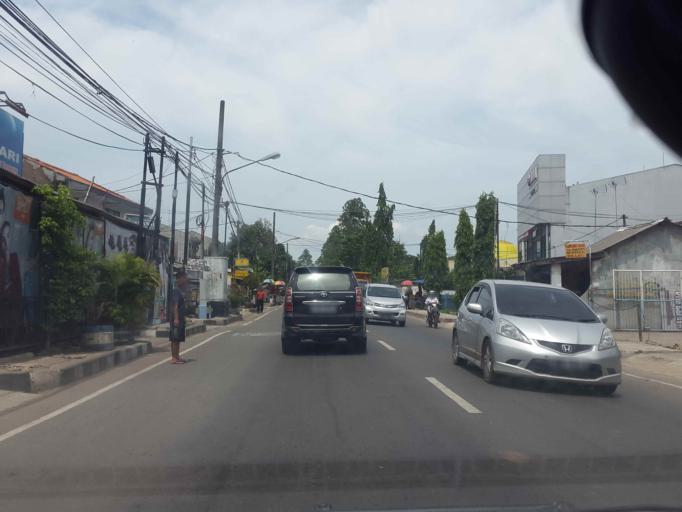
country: ID
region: Banten
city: Tangerang
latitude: -6.1651
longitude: 106.6347
